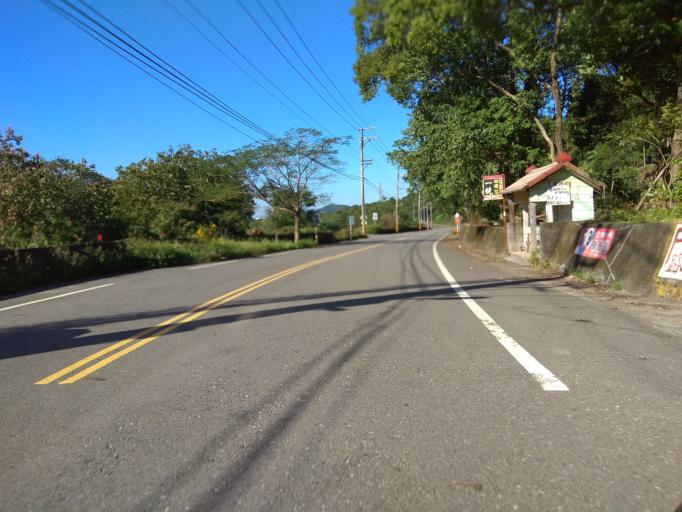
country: TW
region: Taiwan
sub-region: Hsinchu
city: Zhubei
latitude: 24.8454
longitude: 121.1355
